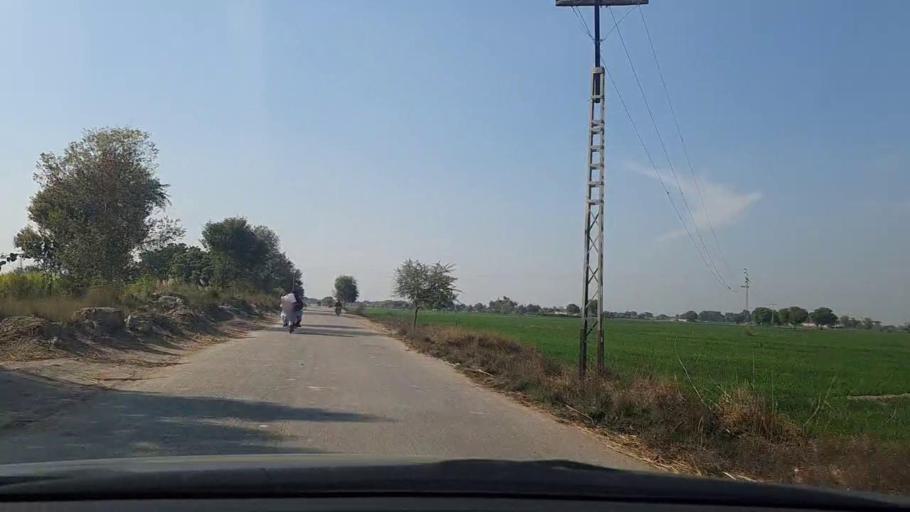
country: PK
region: Sindh
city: Daulatpur
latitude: 26.3118
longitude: 68.0744
